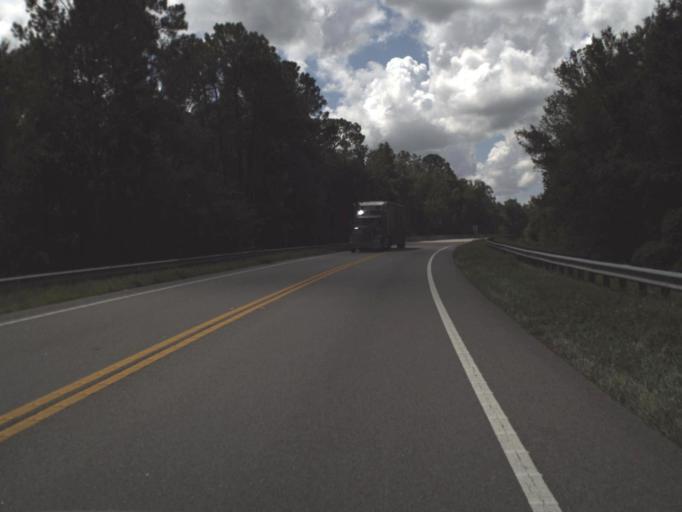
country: US
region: Florida
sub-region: Lake County
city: Four Corners
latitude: 28.3625
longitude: -81.8190
